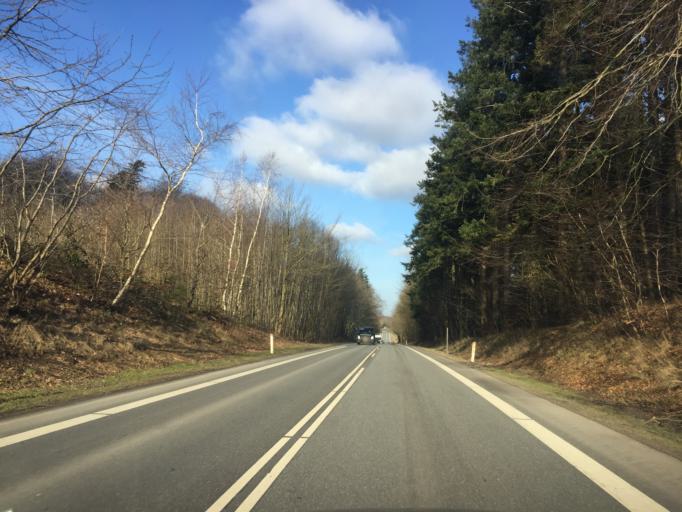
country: DK
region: South Denmark
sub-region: Assens Kommune
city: Vissenbjerg
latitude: 55.4333
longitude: 10.1841
